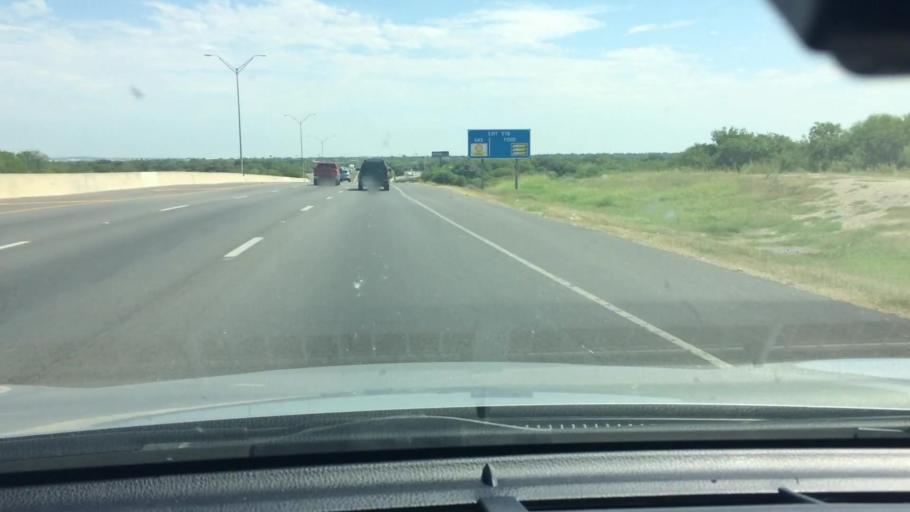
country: US
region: Texas
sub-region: Bexar County
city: San Antonio
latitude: 29.4066
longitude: -98.4392
